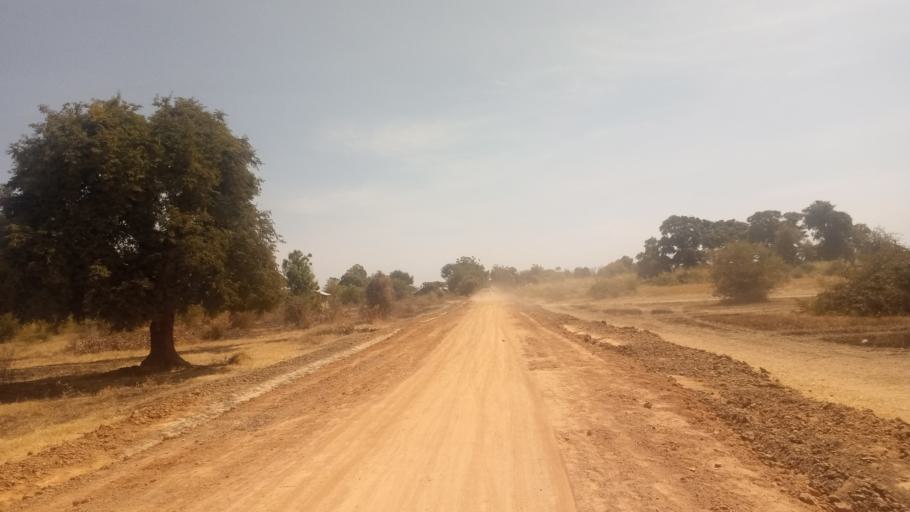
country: NG
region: Adamawa
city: Madagali
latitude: 10.8522
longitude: 13.3906
